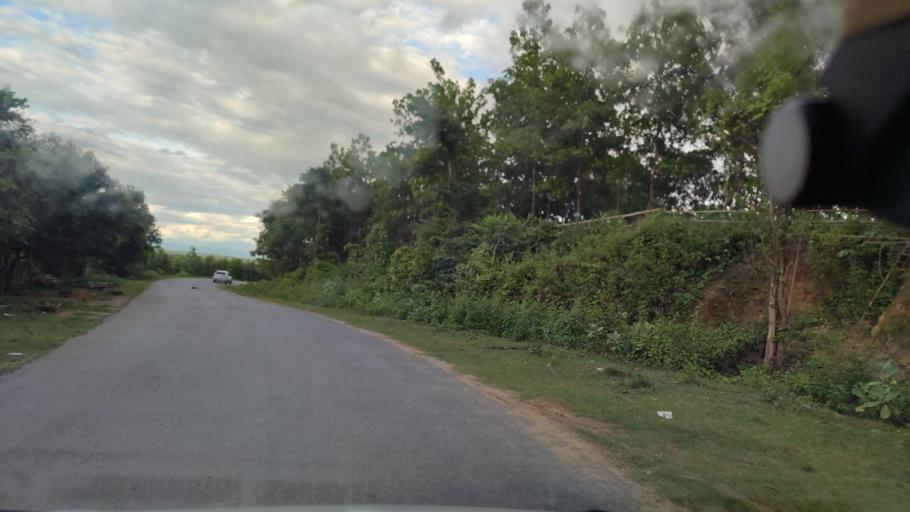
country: MM
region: Magway
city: Taungdwingyi
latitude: 19.9979
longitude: 95.8747
